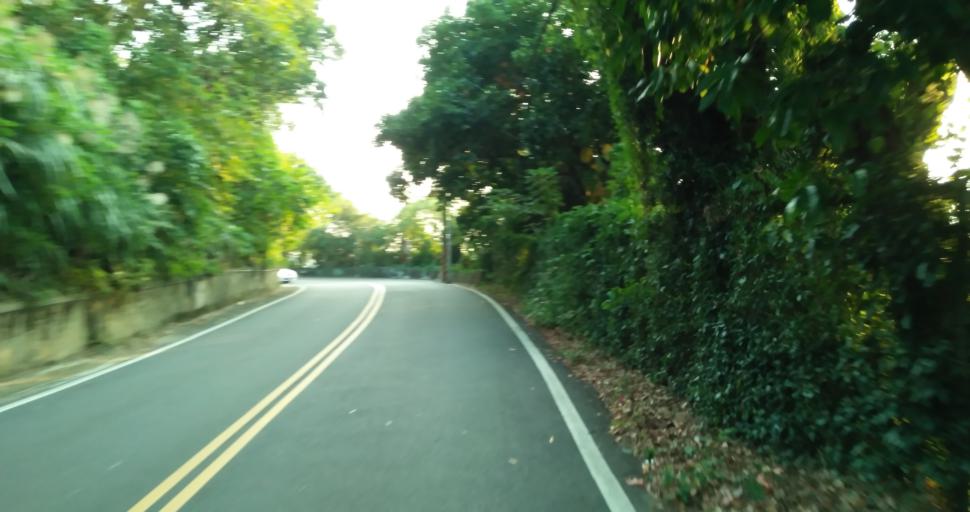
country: TW
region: Taiwan
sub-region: Hsinchu
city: Hsinchu
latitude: 24.7762
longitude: 120.9743
